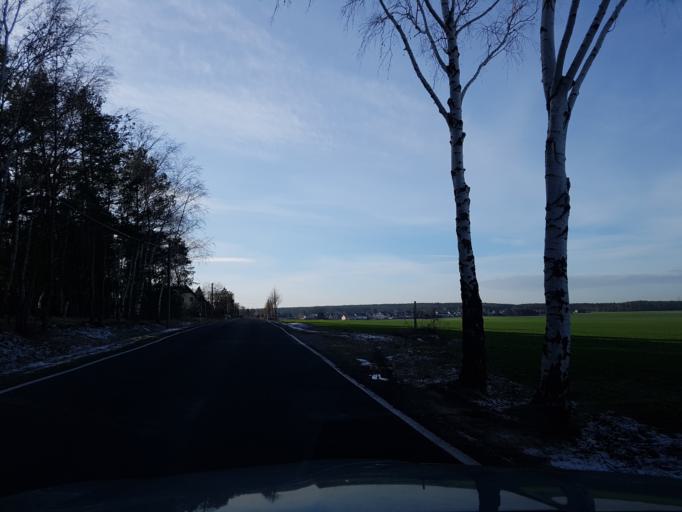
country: DE
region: Brandenburg
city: Schonborn
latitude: 51.5465
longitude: 13.4798
